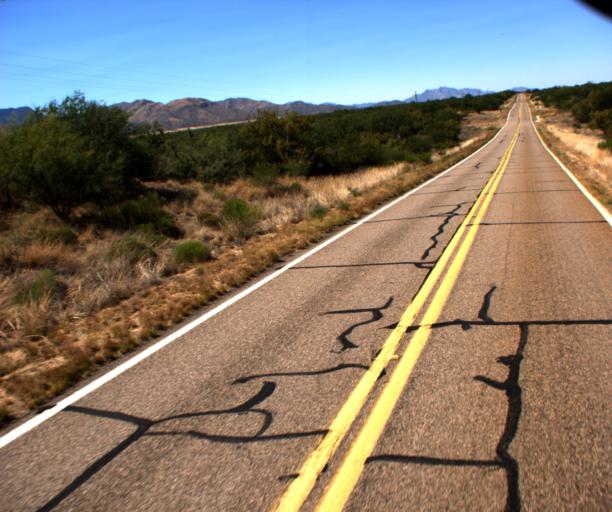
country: US
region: Arizona
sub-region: Pima County
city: Three Points
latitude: 31.7131
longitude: -111.4878
